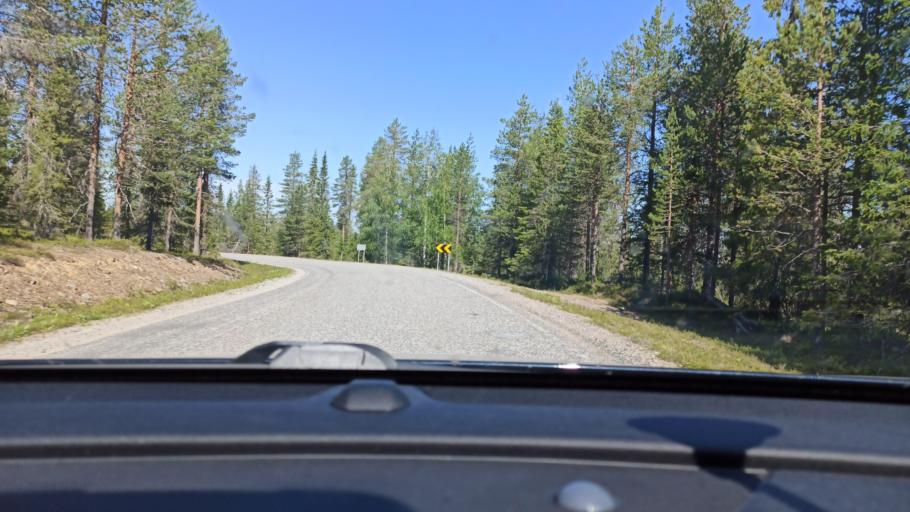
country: FI
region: Lapland
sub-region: Tunturi-Lappi
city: Kolari
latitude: 67.6819
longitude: 24.1368
